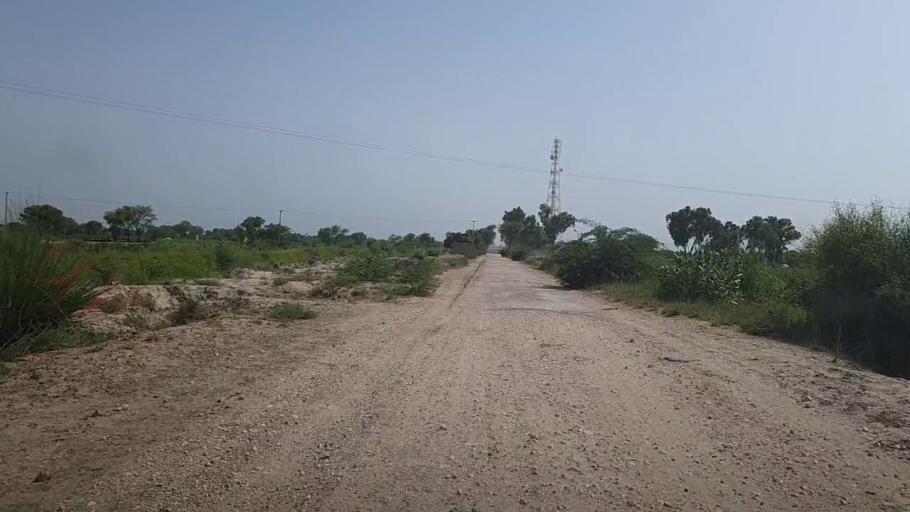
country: PK
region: Sindh
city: Pad Idan
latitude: 26.7824
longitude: 68.3235
